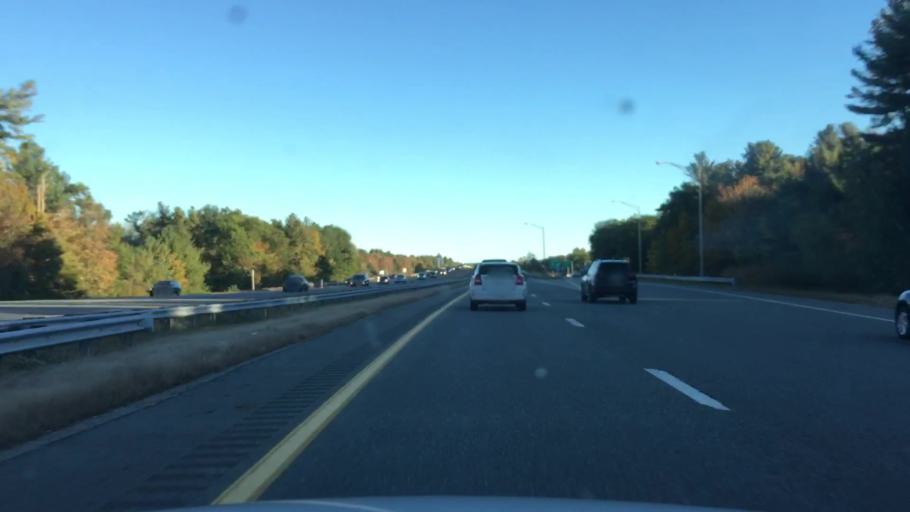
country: US
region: New Hampshire
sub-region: Rockingham County
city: Exeter
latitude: 42.9972
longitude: -70.9319
